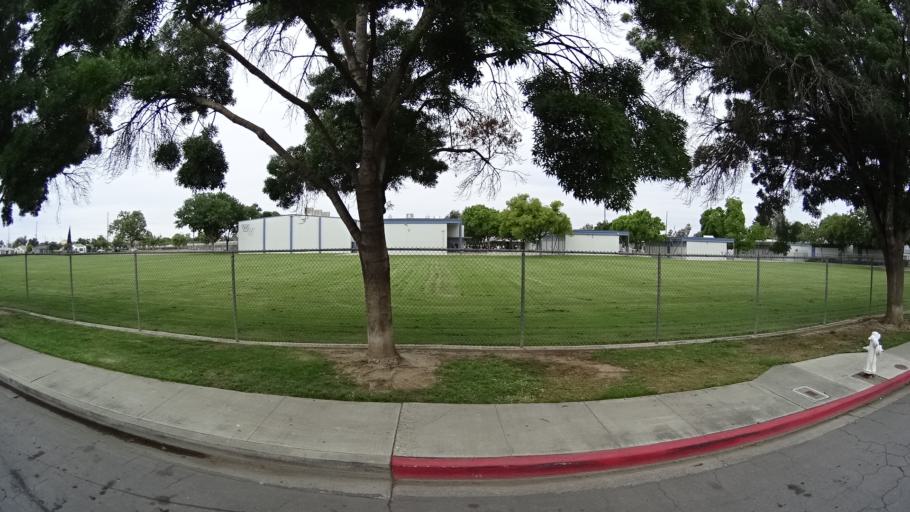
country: US
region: California
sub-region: Kings County
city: Hanford
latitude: 36.3339
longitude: -119.6529
